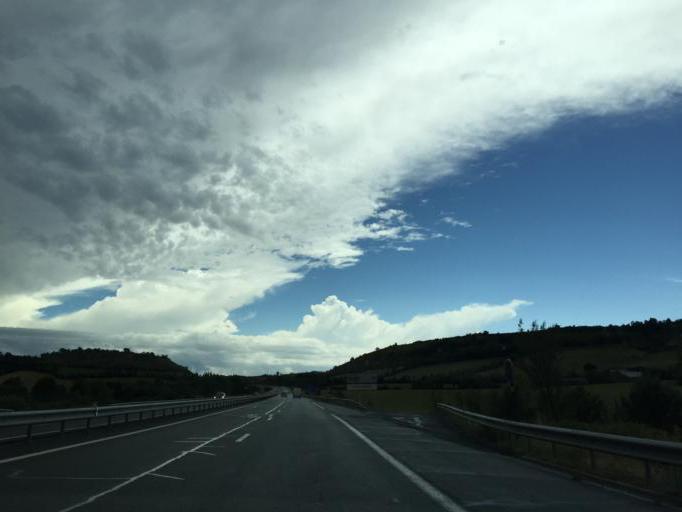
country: FR
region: Midi-Pyrenees
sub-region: Departement de l'Aveyron
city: Severac-le-Chateau
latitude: 44.3251
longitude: 3.0887
